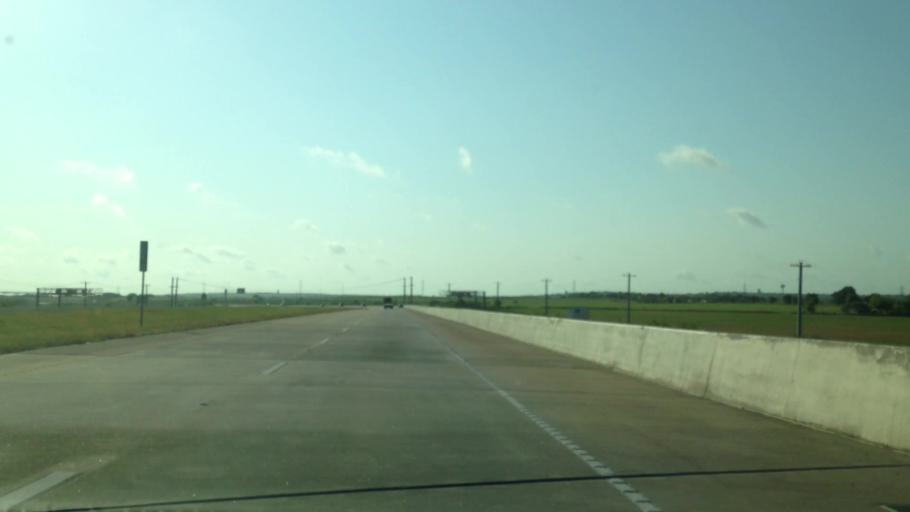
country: US
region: Texas
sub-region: Travis County
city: Onion Creek
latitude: 30.0833
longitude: -97.7350
